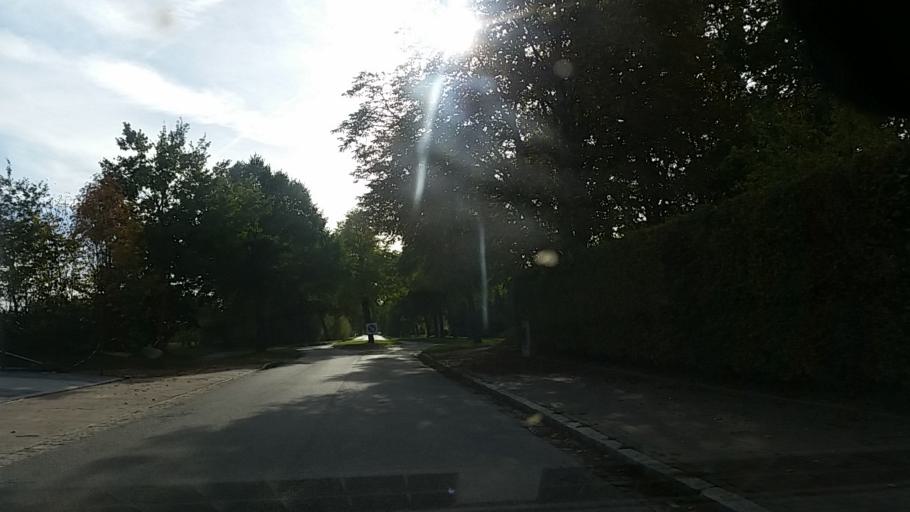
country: DE
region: Schleswig-Holstein
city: Jersbek
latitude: 53.7450
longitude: 10.2128
